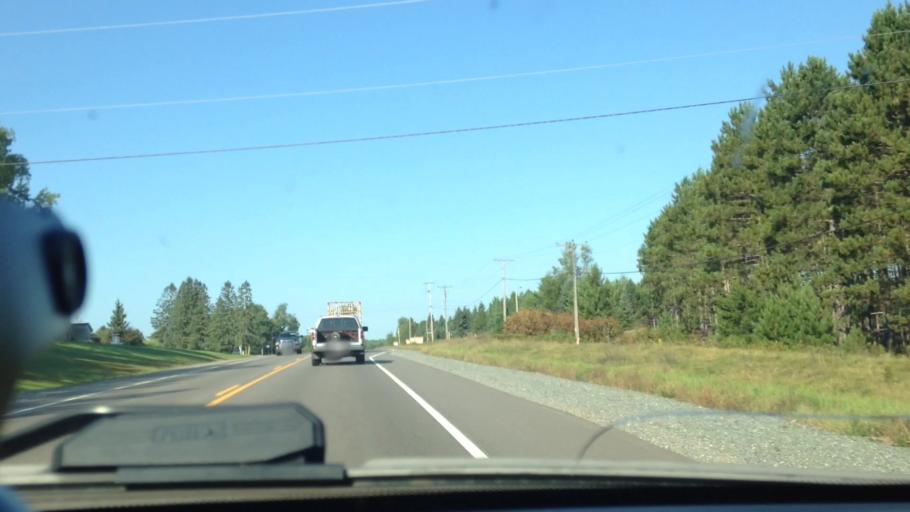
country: US
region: Michigan
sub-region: Dickinson County
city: Iron Mountain
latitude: 45.8760
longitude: -88.1059
